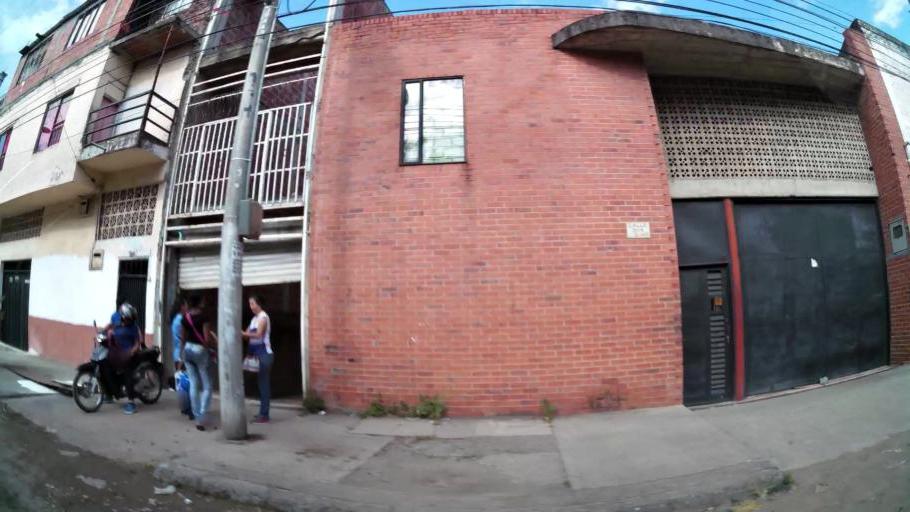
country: CO
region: Valle del Cauca
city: Cali
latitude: 3.4633
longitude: -76.5189
